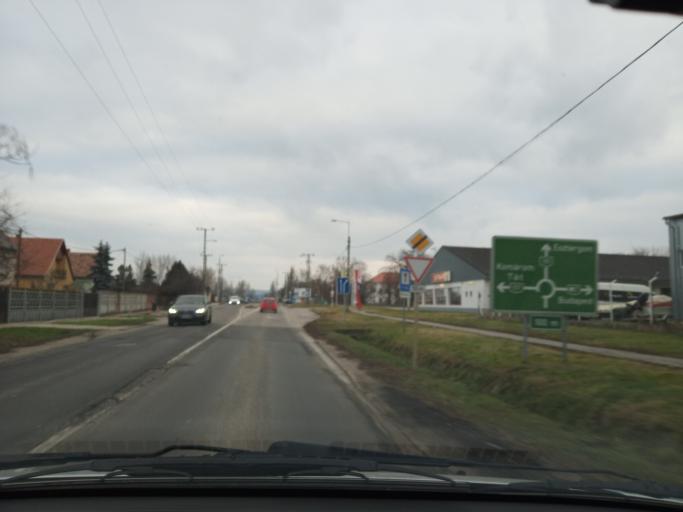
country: HU
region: Komarom-Esztergom
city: Dorog
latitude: 47.7476
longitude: 18.7303
